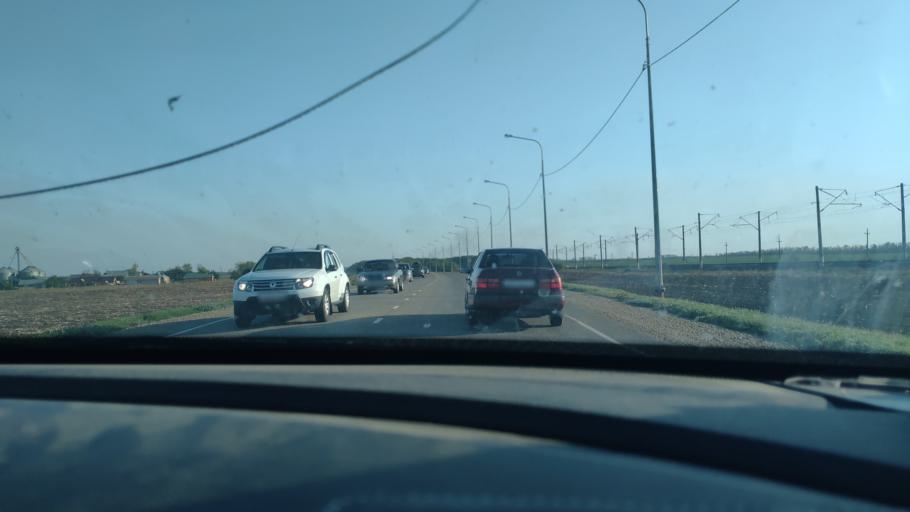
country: RU
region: Krasnodarskiy
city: Novominskaya
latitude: 46.3076
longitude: 38.9305
